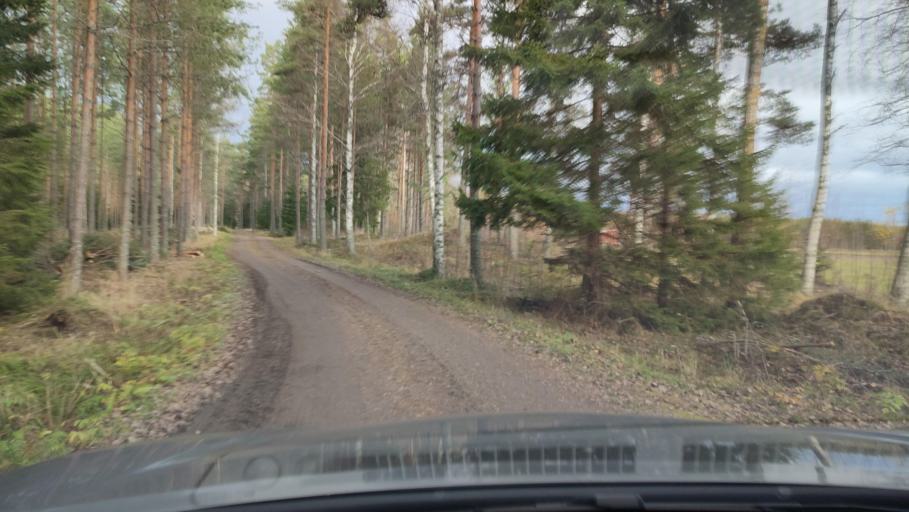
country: FI
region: Southern Ostrobothnia
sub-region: Suupohja
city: Karijoki
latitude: 62.2427
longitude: 21.5787
